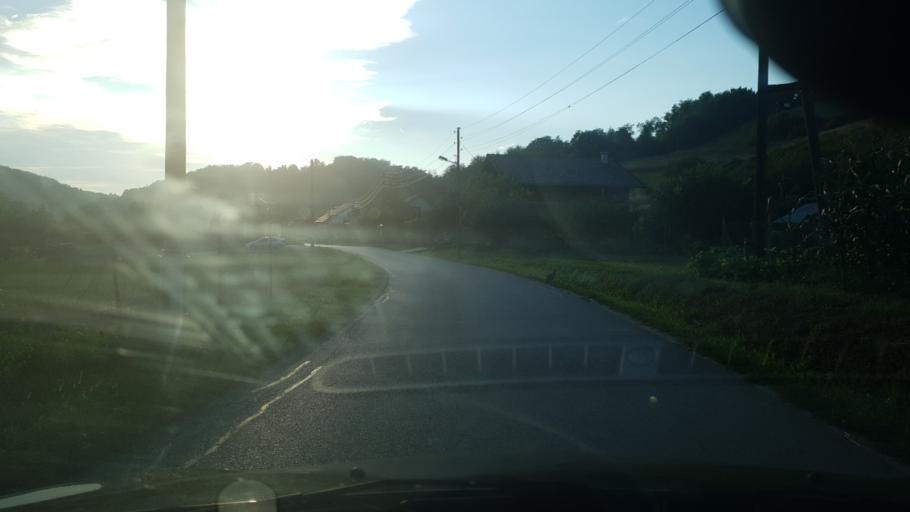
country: HR
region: Krapinsko-Zagorska
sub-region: Grad Krapina
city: Krapina
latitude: 46.1016
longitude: 15.8733
